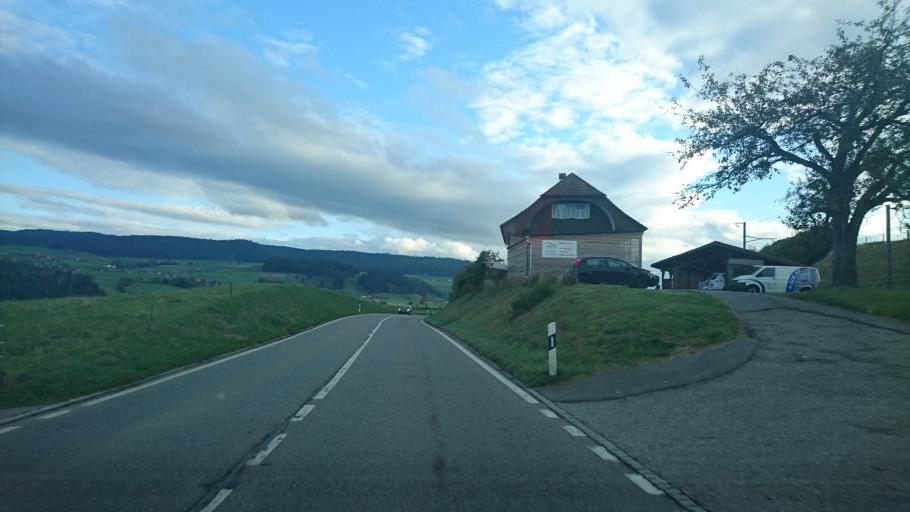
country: CH
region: Bern
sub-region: Bern-Mittelland District
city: Konolfingen
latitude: 46.8985
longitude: 7.6336
